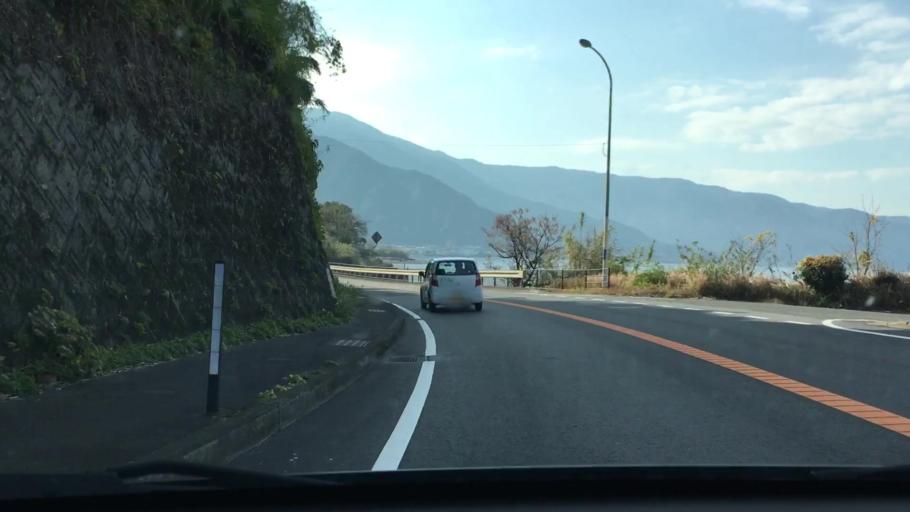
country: JP
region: Kagoshima
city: Hamanoichi
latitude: 31.5982
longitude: 130.7879
